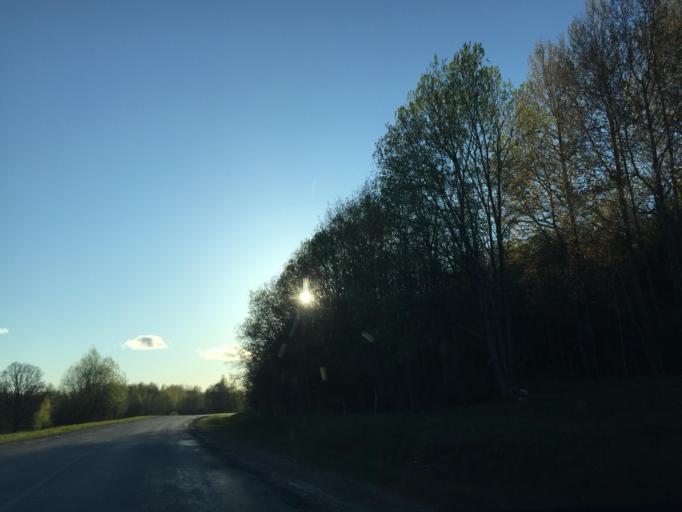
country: LV
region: Vecpiebalga
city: Vecpiebalga
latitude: 56.8414
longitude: 25.9455
